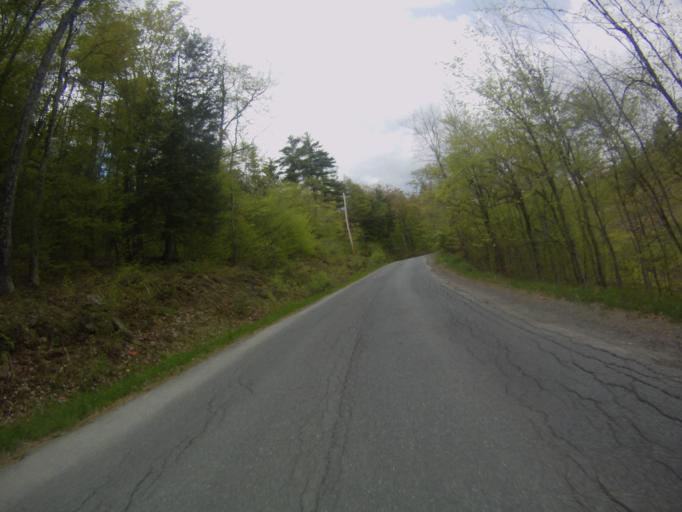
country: US
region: New York
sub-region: Essex County
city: Ticonderoga
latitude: 43.8847
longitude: -73.4807
